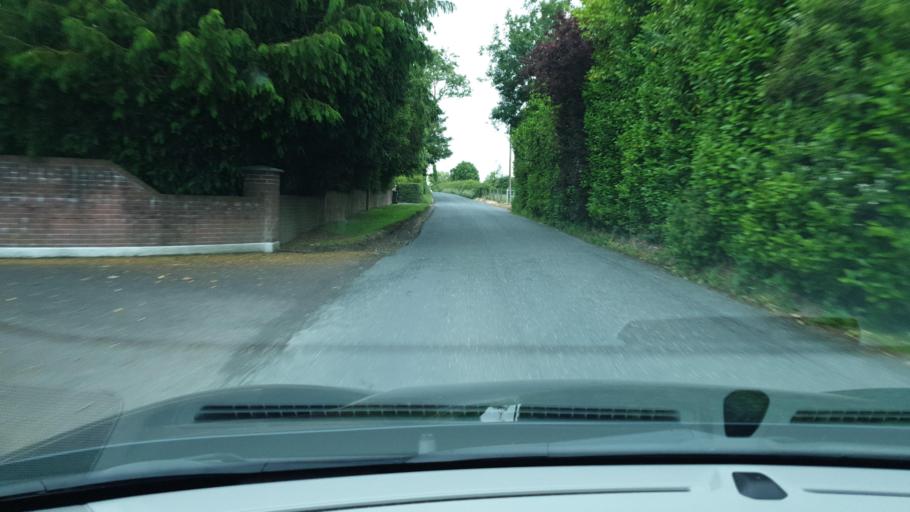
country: IE
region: Leinster
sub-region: An Mhi
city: Navan
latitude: 53.6251
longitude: -6.7002
